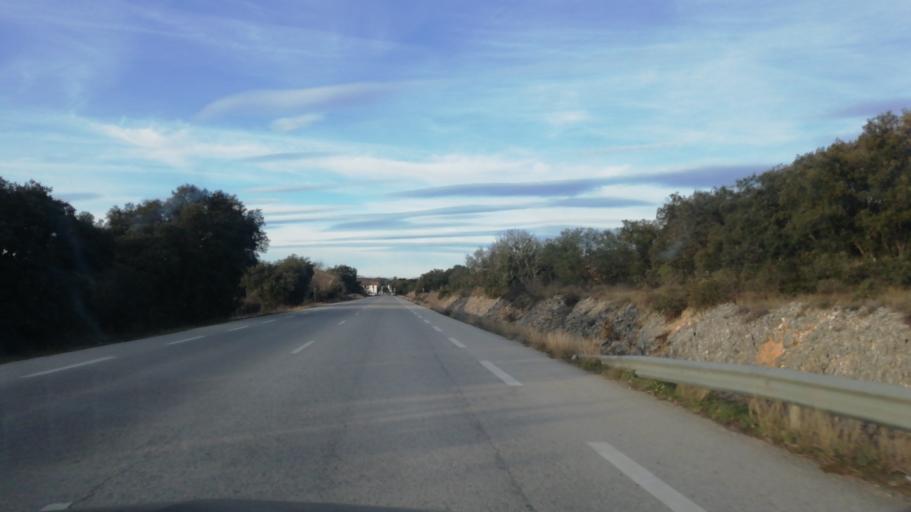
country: FR
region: Languedoc-Roussillon
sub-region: Departement du Gard
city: Quissac
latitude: 43.8989
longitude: 4.0070
